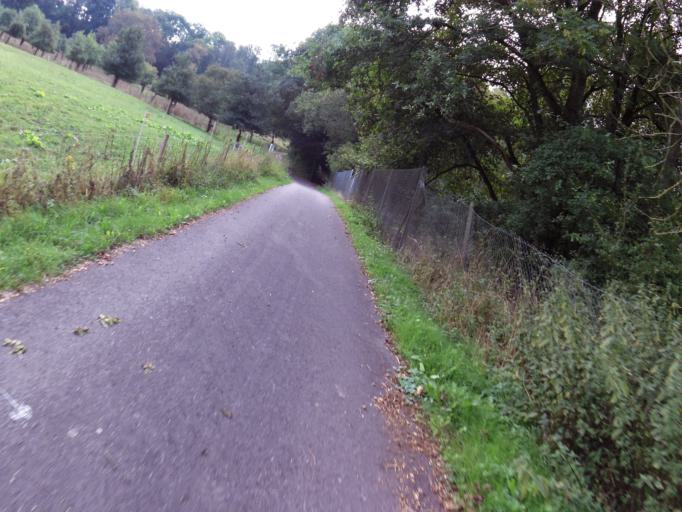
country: DE
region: Rheinland-Pfalz
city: Metterich
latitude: 49.9753
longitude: 6.5837
